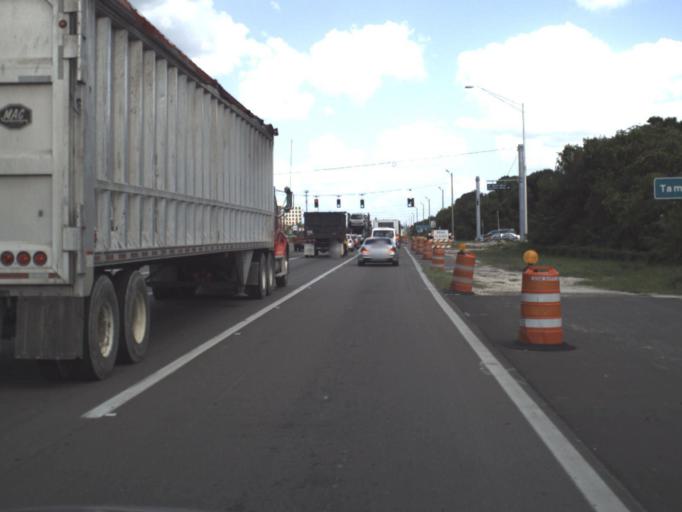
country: US
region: Florida
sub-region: Pinellas County
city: Feather Sound
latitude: 27.8937
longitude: -82.6694
